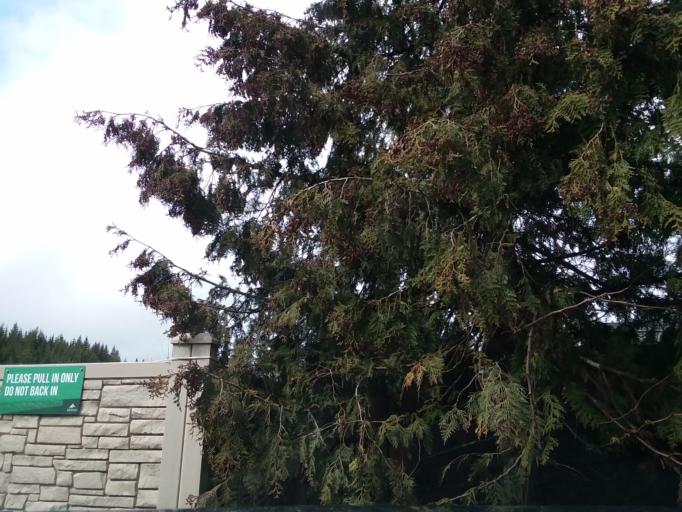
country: CA
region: British Columbia
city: Whistler
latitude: 50.1304
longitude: -122.9545
